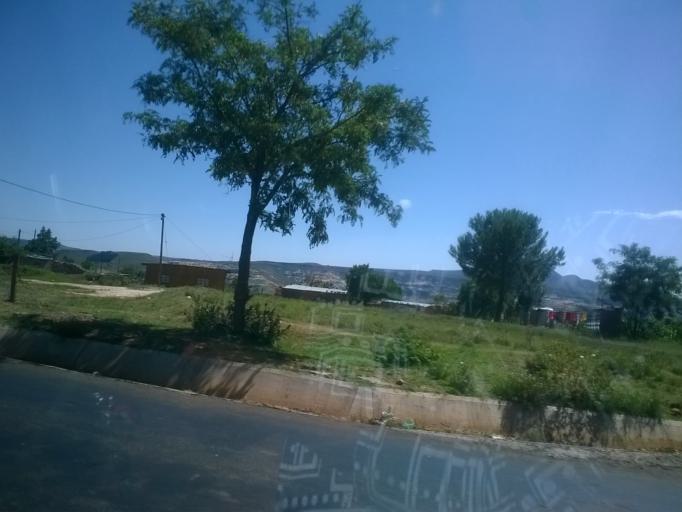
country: LS
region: Berea
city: Teyateyaneng
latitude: -29.1047
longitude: 27.9615
